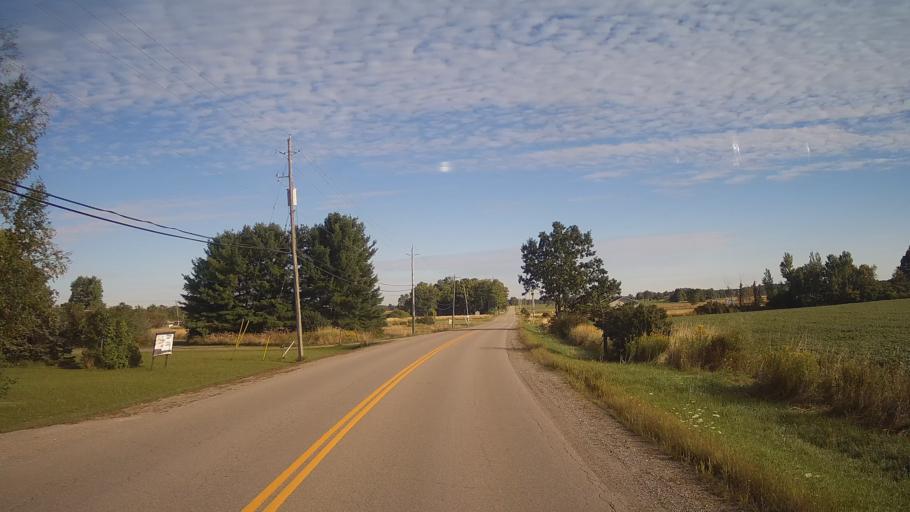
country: CA
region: Ontario
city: Gananoque
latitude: 44.3671
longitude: -76.1380
